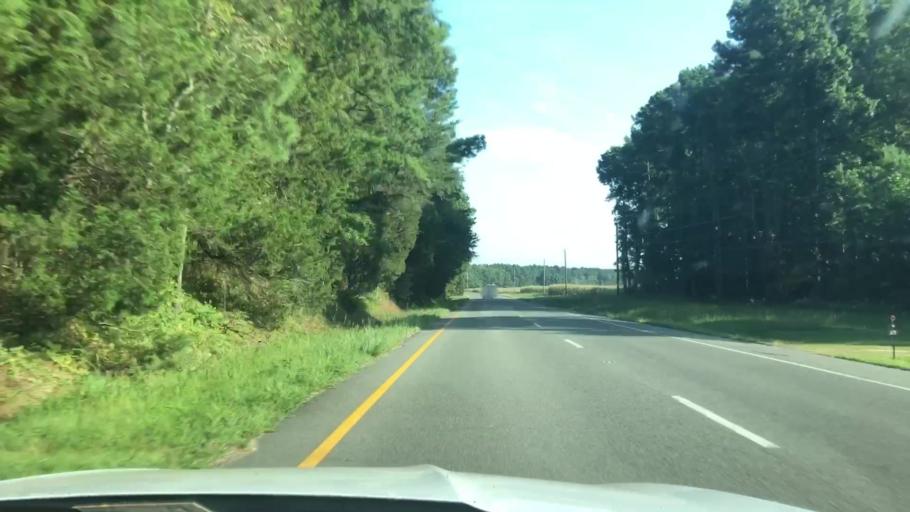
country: US
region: Virginia
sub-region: King and Queen County
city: King and Queen Court House
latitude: 37.7470
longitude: -76.7207
